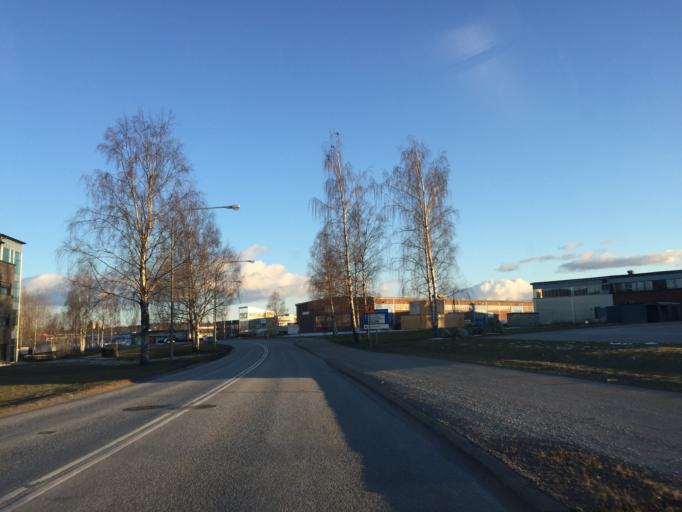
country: SE
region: OErebro
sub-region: Orebro Kommun
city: Orebro
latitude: 59.2591
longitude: 15.1760
